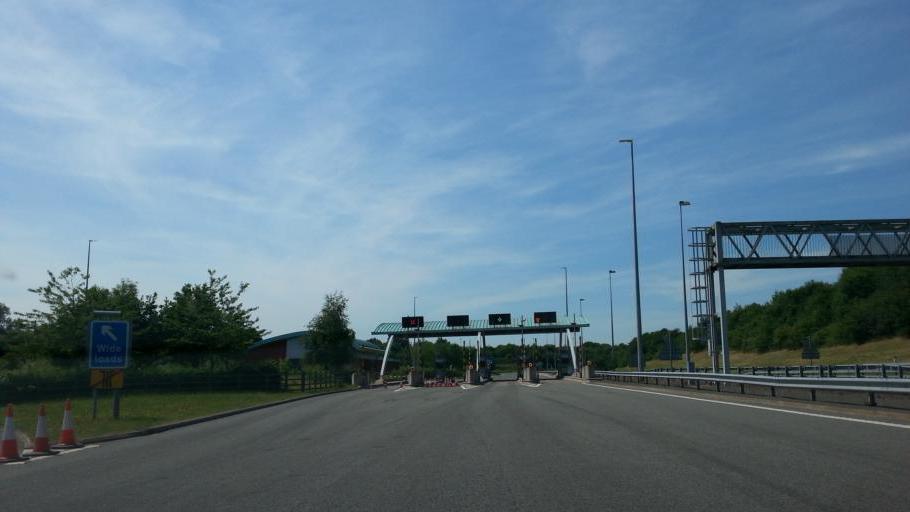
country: GB
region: England
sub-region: Staffordshire
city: Chasetown
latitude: 52.6648
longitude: -1.9302
